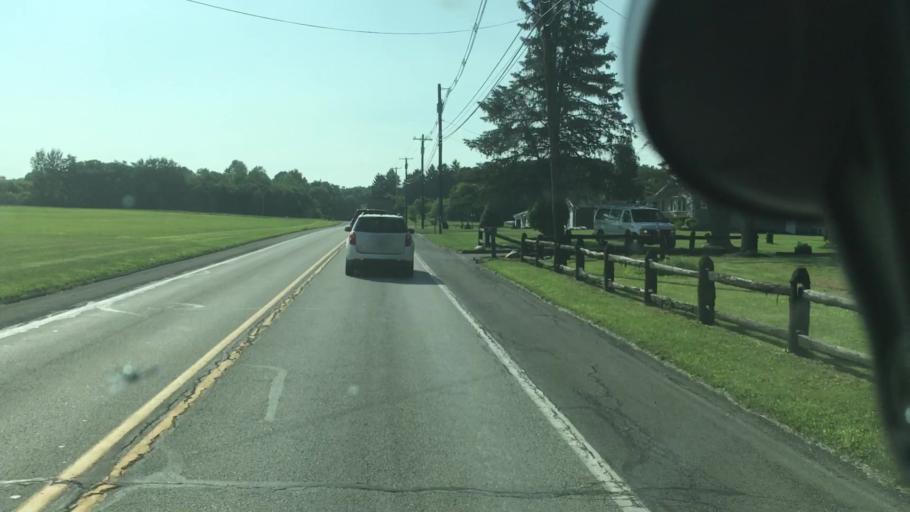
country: US
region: Pennsylvania
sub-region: Lawrence County
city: Oakwood
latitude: 41.0221
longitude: -80.4227
